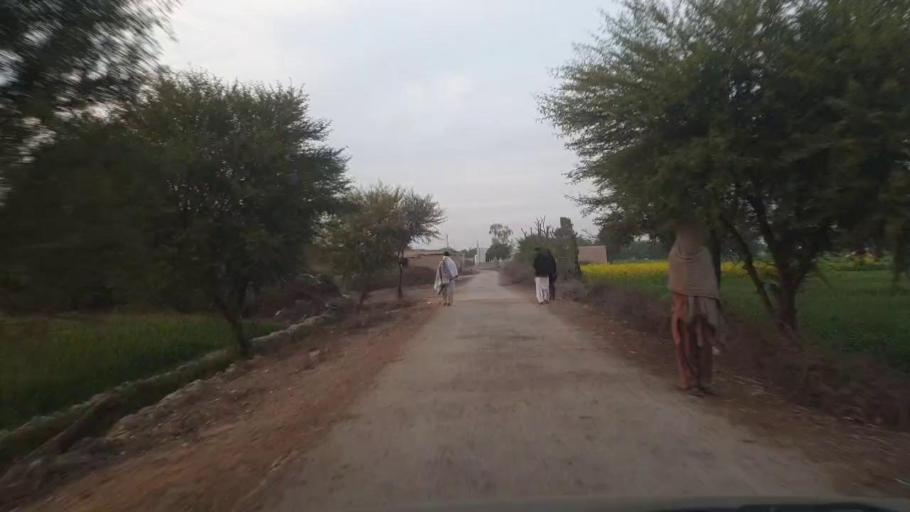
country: PK
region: Sindh
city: Shahpur Chakar
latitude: 26.0677
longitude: 68.5363
